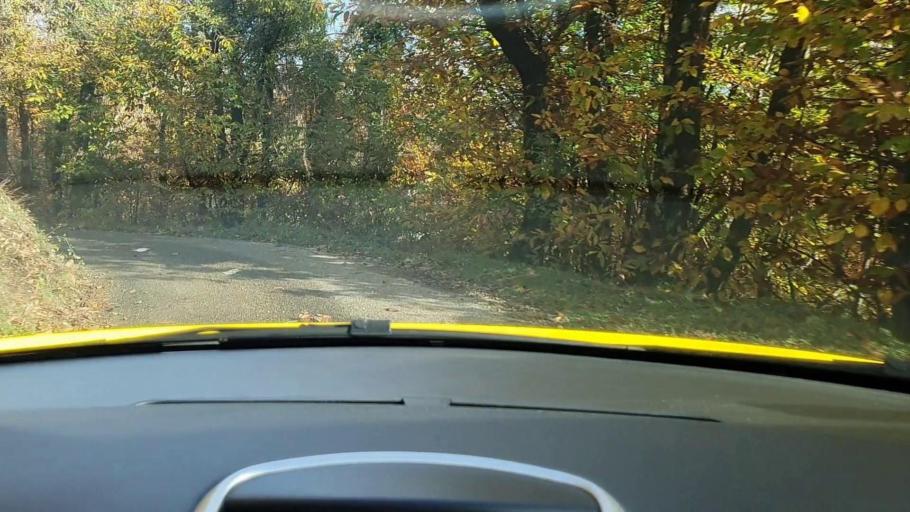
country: FR
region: Languedoc-Roussillon
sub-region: Departement du Gard
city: Valleraugue
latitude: 44.0875
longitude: 3.7427
